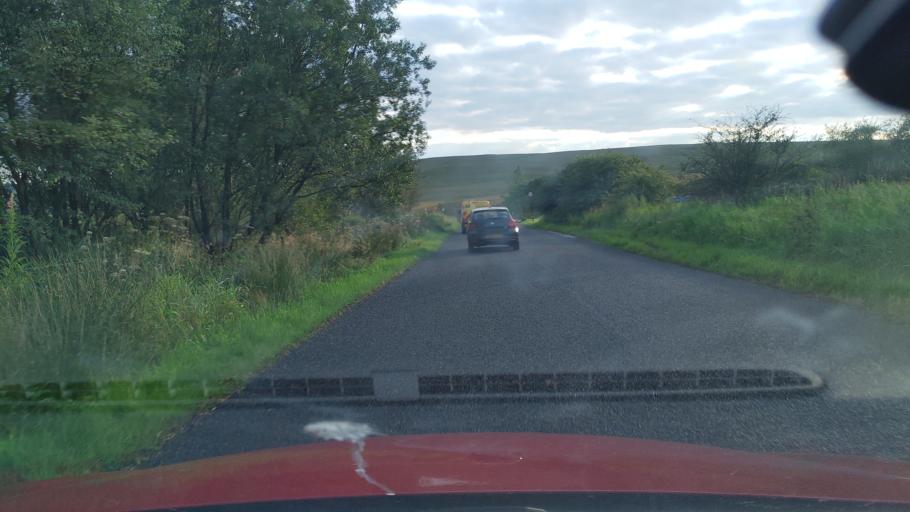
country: GB
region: England
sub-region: Blackburn with Darwen
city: Darwen
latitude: 53.6680
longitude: -2.5071
